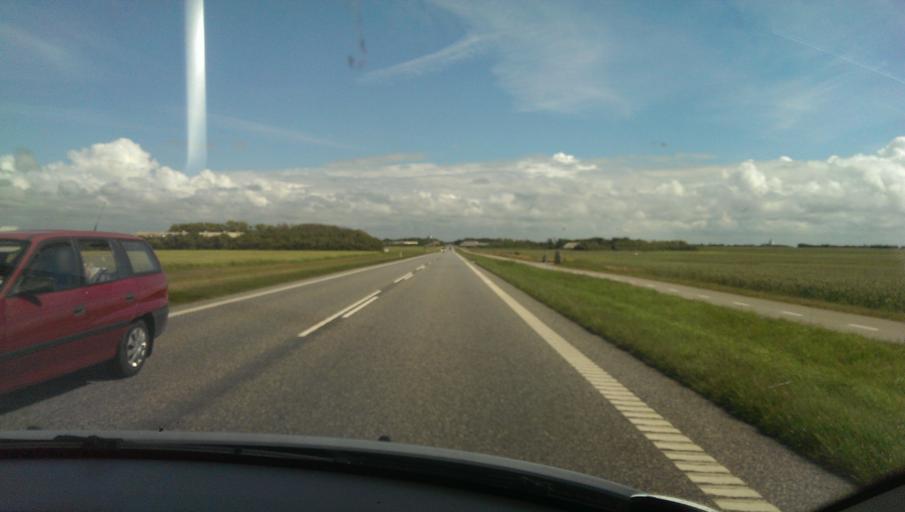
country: DK
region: Central Jutland
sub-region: Ringkobing-Skjern Kommune
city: Ringkobing
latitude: 56.1108
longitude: 8.1928
